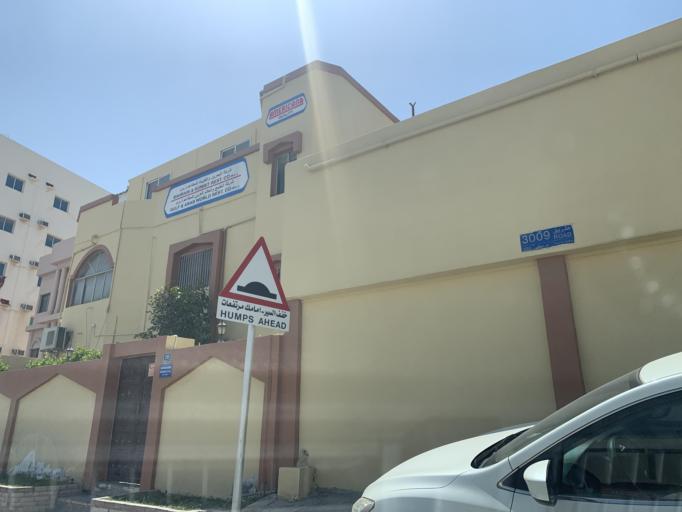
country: BH
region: Manama
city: Manama
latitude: 26.2124
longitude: 50.5714
